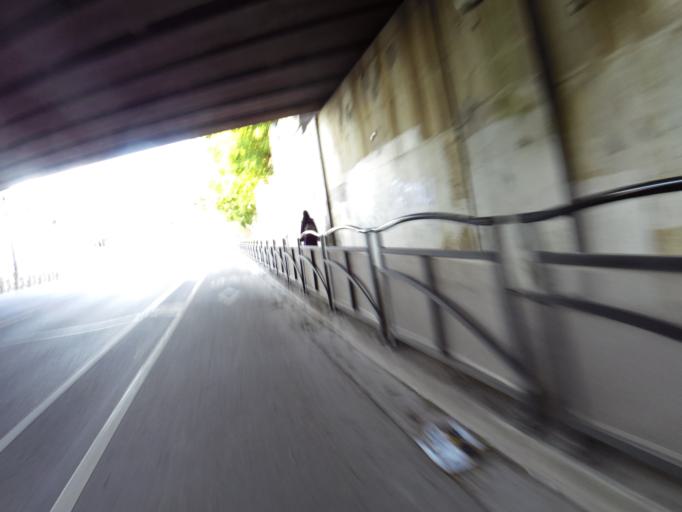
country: CA
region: Ontario
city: Toronto
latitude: 43.6474
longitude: -79.4391
